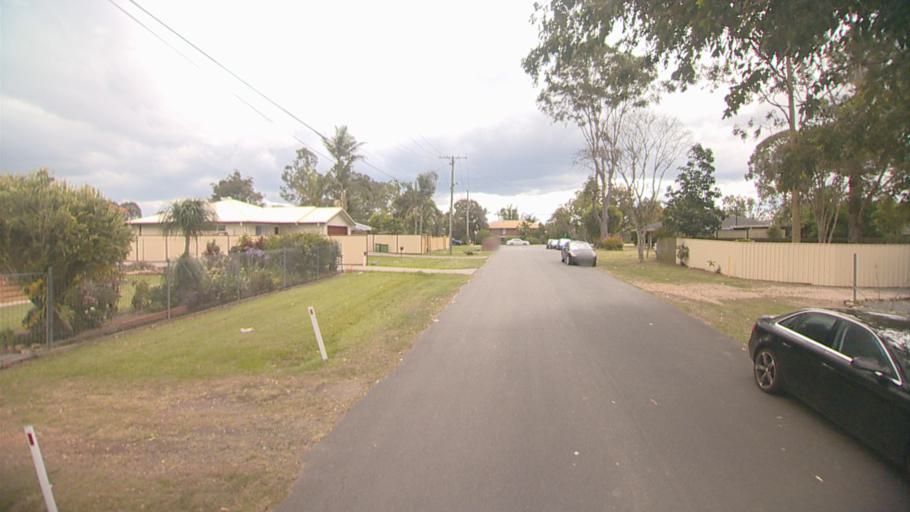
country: AU
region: Queensland
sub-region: Logan
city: Waterford West
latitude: -27.6940
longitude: 153.1370
